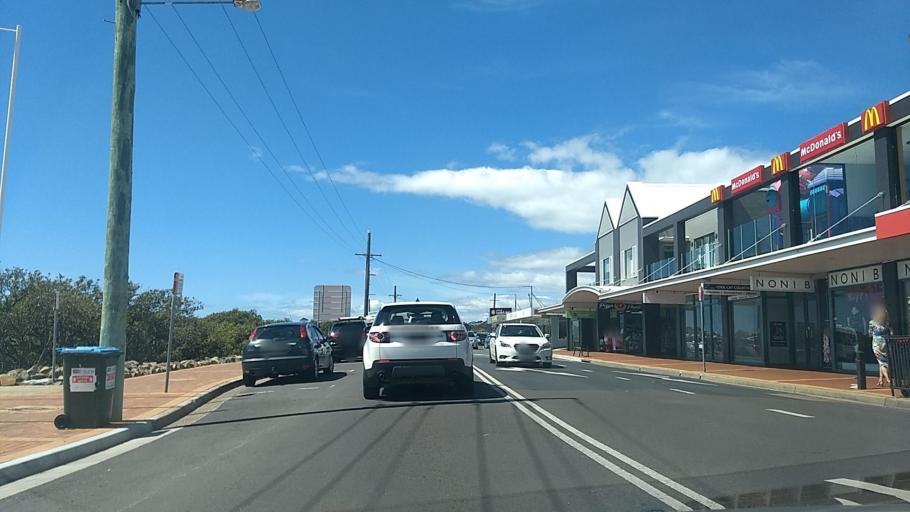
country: AU
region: New South Wales
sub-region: Bega Valley
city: Merimbula
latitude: -36.8898
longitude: 149.9107
